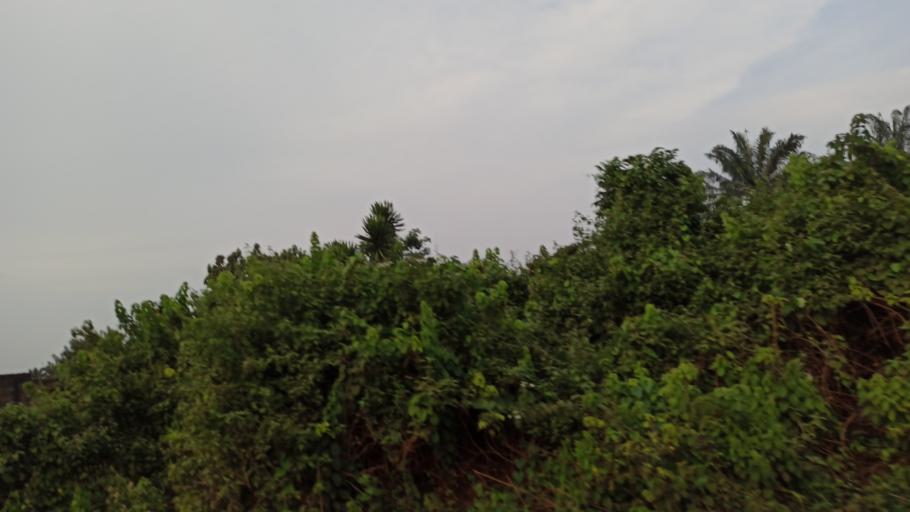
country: BJ
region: Queme
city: Porto-Novo
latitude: 6.5197
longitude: 2.6756
